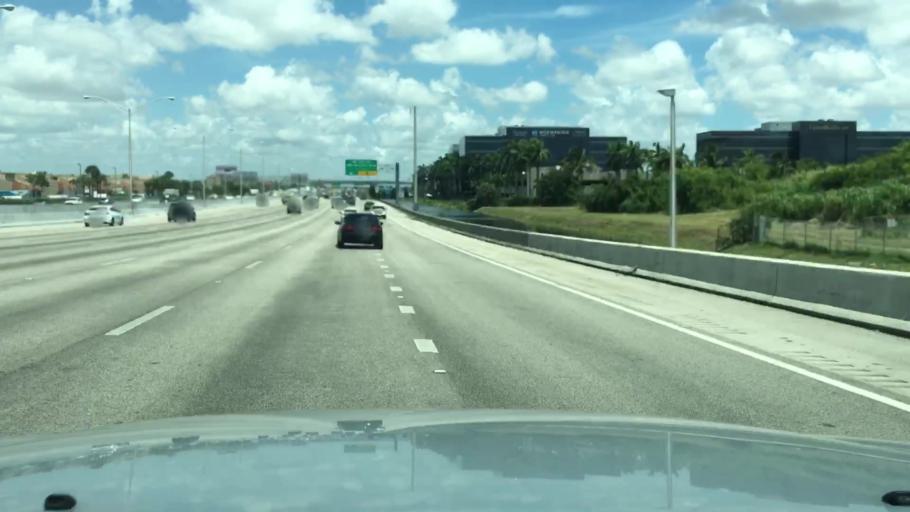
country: US
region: Florida
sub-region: Miami-Dade County
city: Flagami
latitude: 25.7878
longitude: -80.3202
